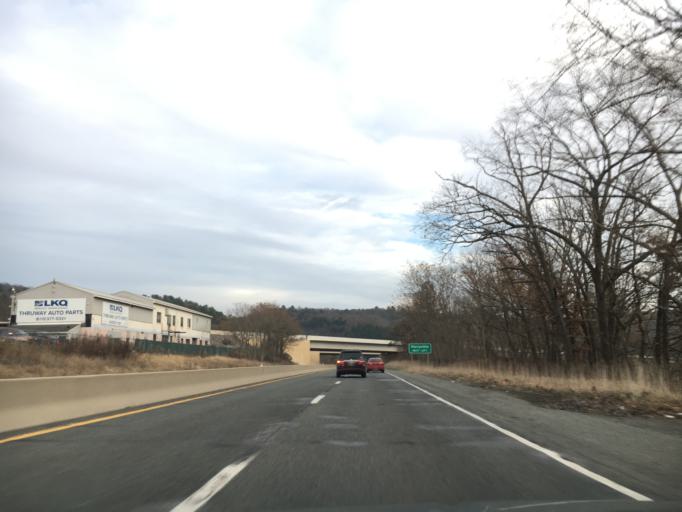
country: US
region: Pennsylvania
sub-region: Carbon County
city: Weissport East
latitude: 40.8190
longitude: -75.6801
